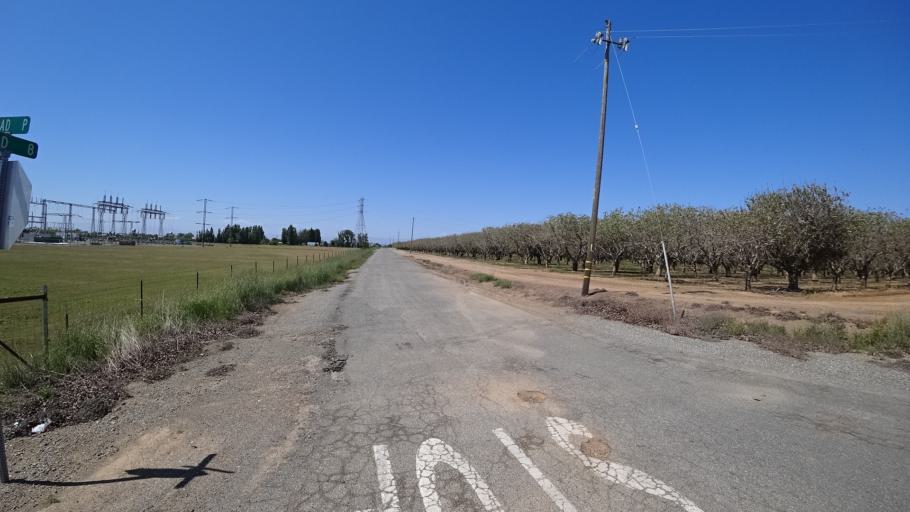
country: US
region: California
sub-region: Glenn County
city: Orland
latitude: 39.7794
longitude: -122.1411
